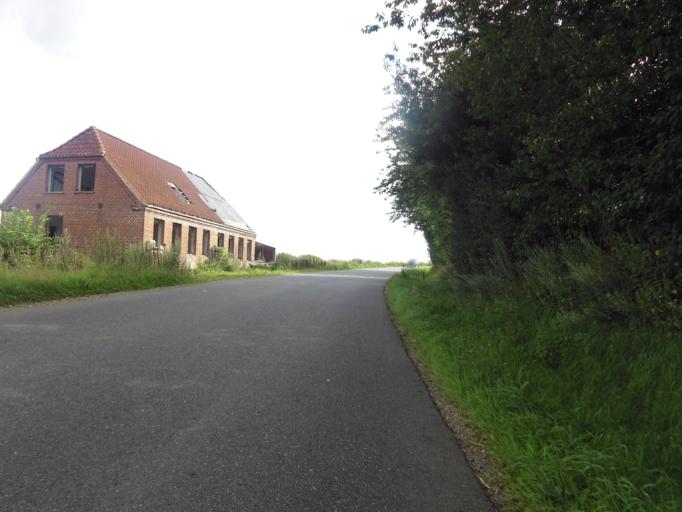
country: DK
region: South Denmark
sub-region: Haderslev Kommune
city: Haderslev
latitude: 55.2367
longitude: 9.4680
